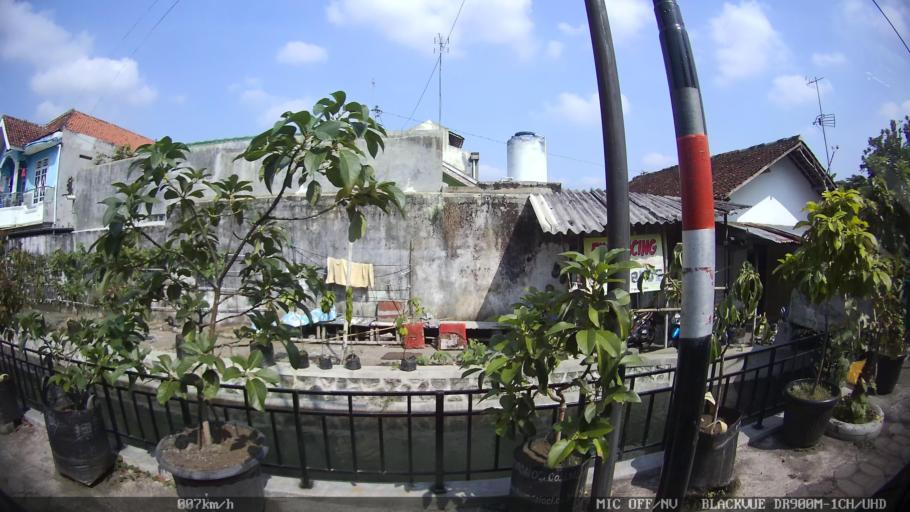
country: ID
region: Daerah Istimewa Yogyakarta
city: Yogyakarta
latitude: -7.8067
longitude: 110.3746
